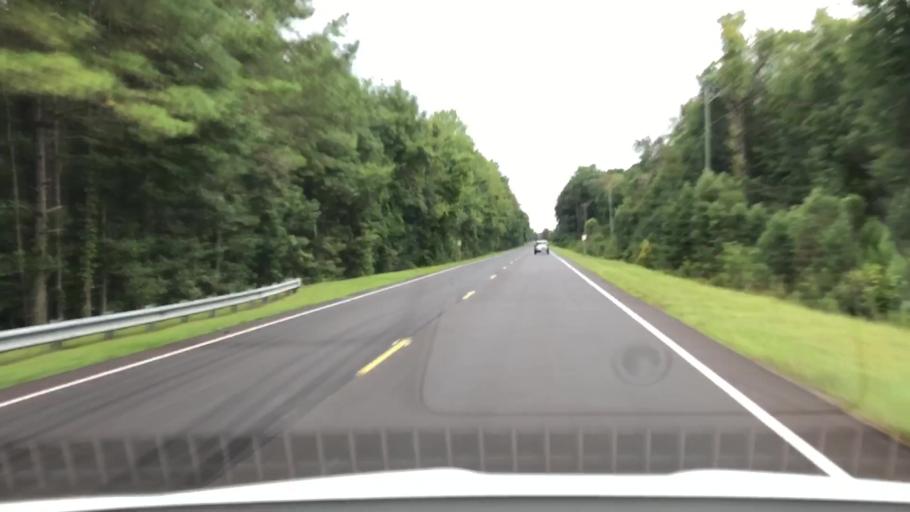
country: US
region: North Carolina
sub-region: Jones County
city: Maysville
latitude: 34.8721
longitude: -77.1969
